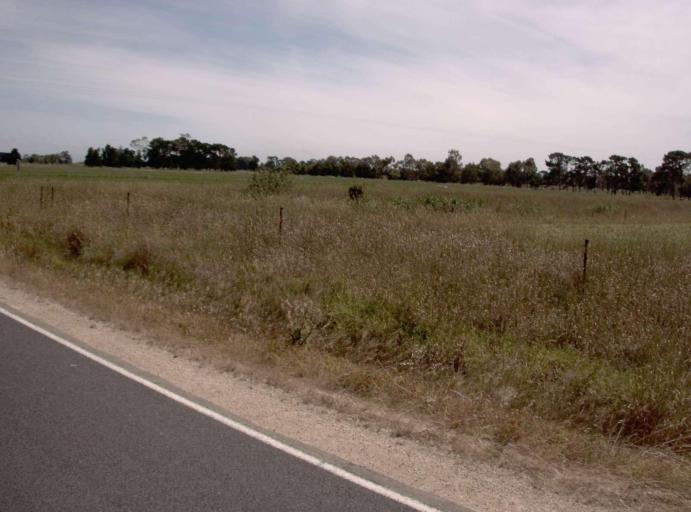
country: AU
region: Victoria
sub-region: Wellington
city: Heyfield
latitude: -38.0349
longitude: 146.8783
